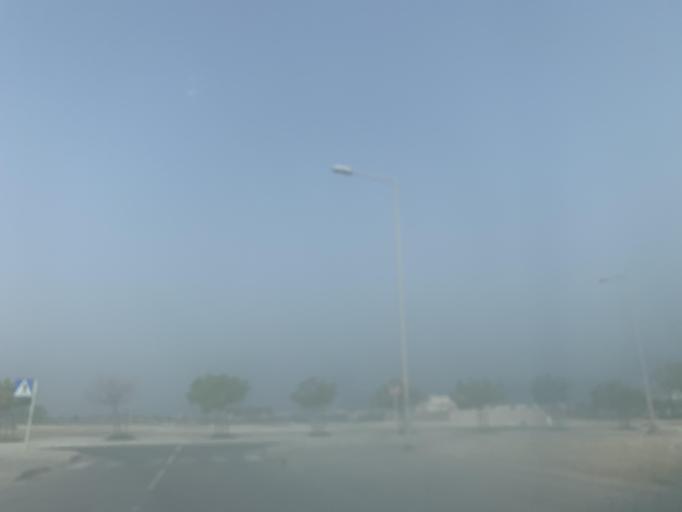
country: BH
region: Manama
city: Jidd Hafs
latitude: 26.2296
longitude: 50.4518
